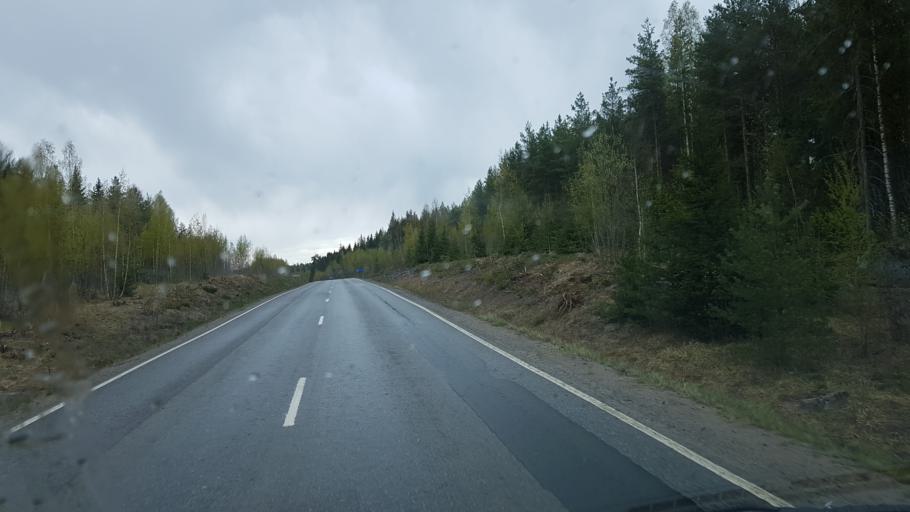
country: FI
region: Pirkanmaa
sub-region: Tampere
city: Pirkkala
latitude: 61.4039
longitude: 23.6318
